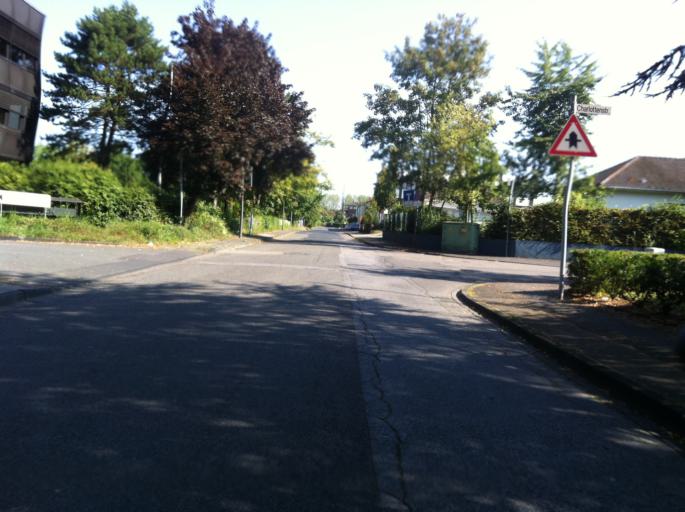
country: DE
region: North Rhine-Westphalia
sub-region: Regierungsbezirk Koln
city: Ostheim
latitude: 50.9053
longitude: 7.0280
